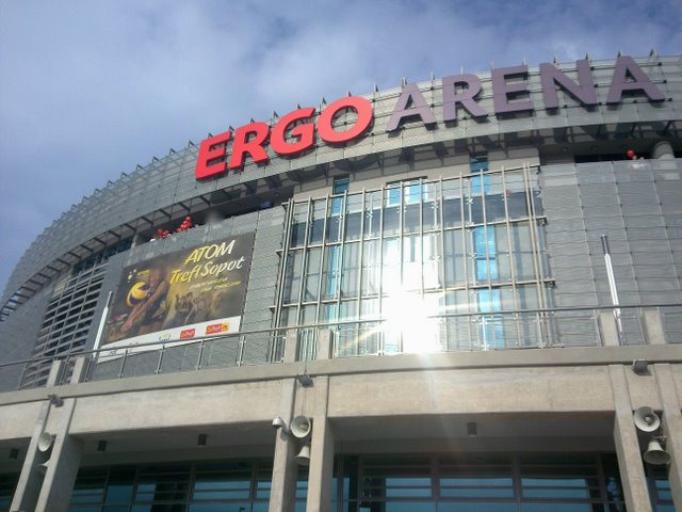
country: PL
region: Pomeranian Voivodeship
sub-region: Sopot
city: Sopot
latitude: 54.4259
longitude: 18.5790
